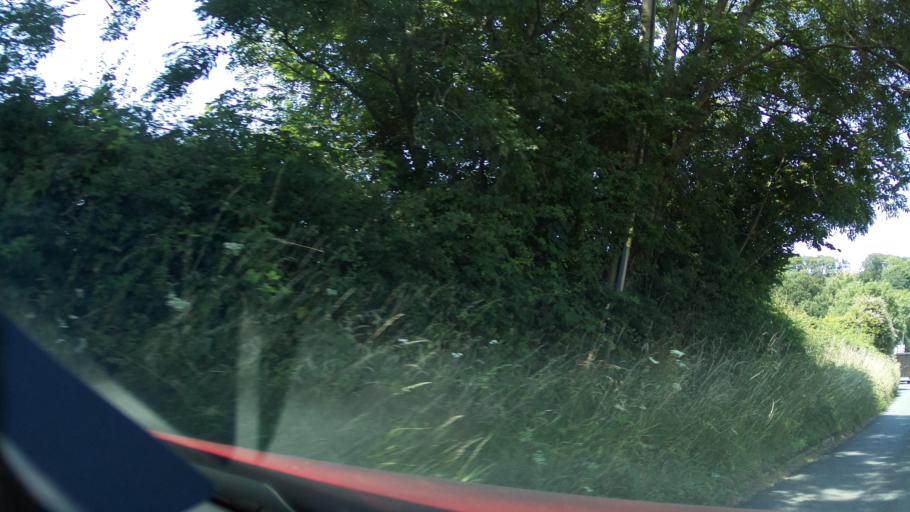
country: GB
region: Wales
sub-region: Caerphilly County Borough
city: Caerphilly
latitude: 51.5479
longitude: -3.2085
